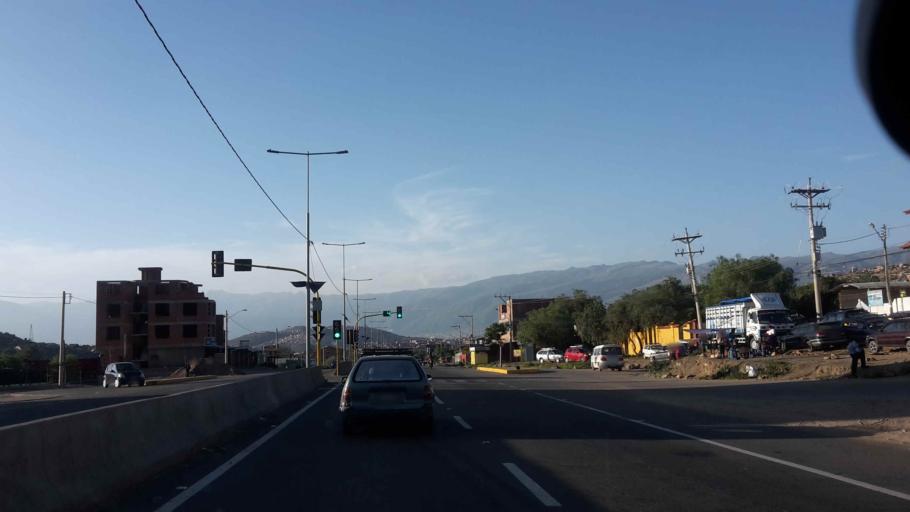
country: BO
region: Cochabamba
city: Cochabamba
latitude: -17.4822
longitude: -66.1095
